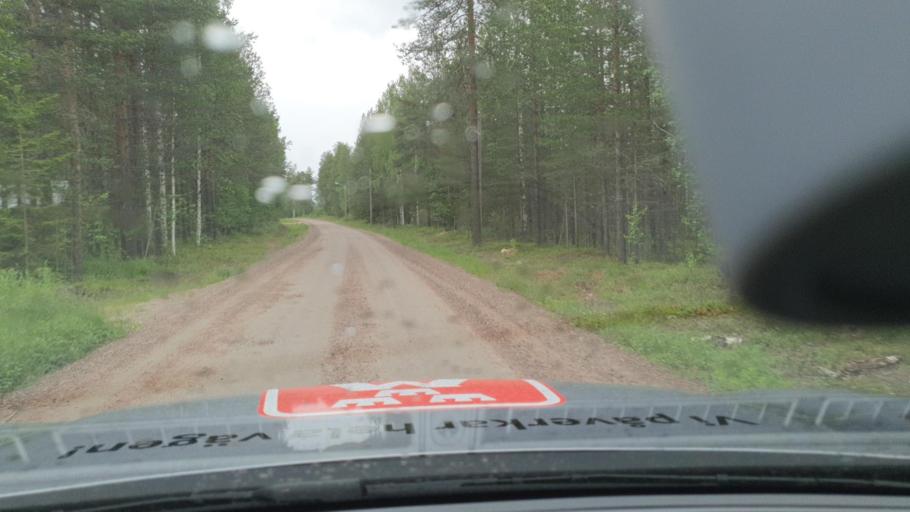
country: SE
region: Norrbotten
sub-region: Overkalix Kommun
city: OEverkalix
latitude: 66.4967
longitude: 22.7621
